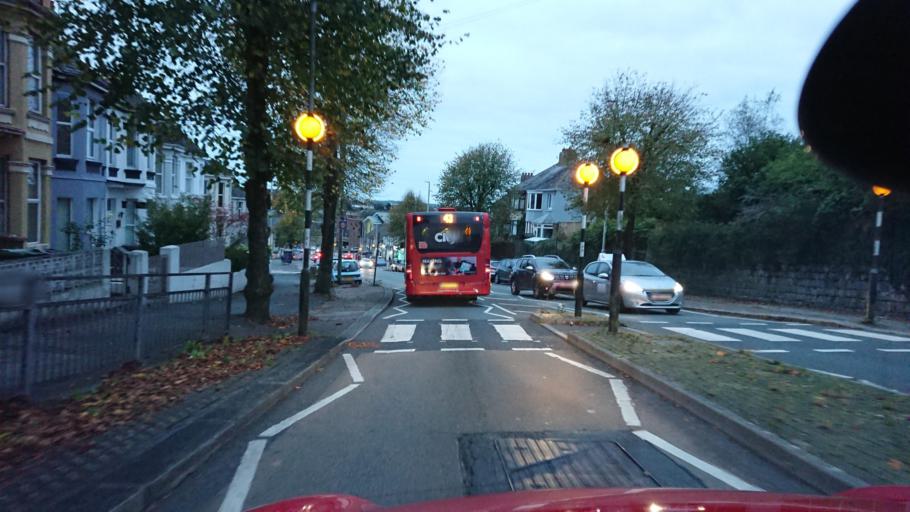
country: GB
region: England
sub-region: Cornwall
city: Torpoint
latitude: 50.4067
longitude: -4.1859
